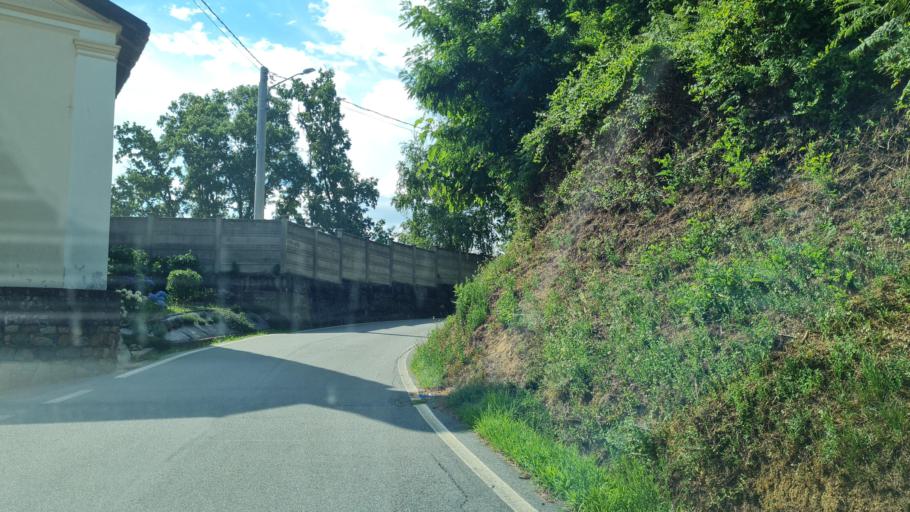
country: IT
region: Piedmont
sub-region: Provincia di Biella
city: Lessona
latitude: 45.5817
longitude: 8.2088
